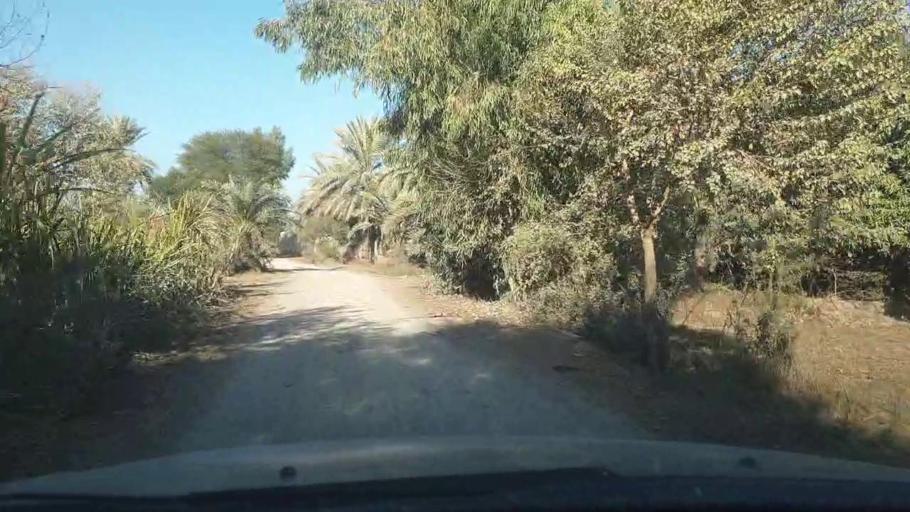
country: PK
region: Sindh
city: Adilpur
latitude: 27.9600
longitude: 69.2022
